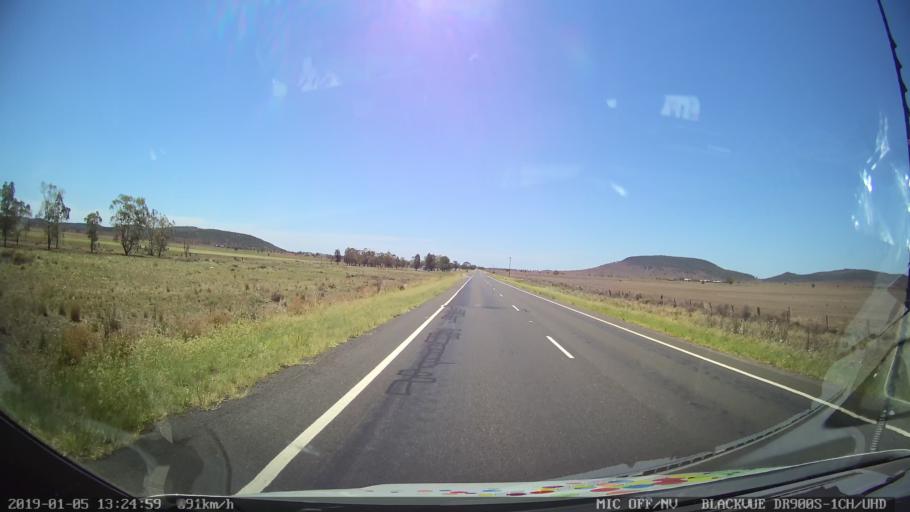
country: AU
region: New South Wales
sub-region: Gunnedah
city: Gunnedah
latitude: -31.0650
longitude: 149.9962
